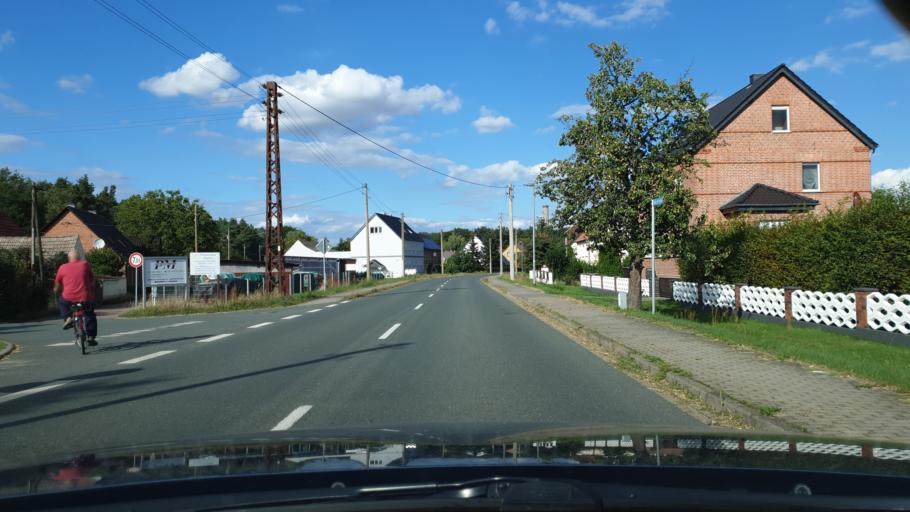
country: DE
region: Saxony-Anhalt
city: Radis
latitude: 51.7535
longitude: 12.5193
